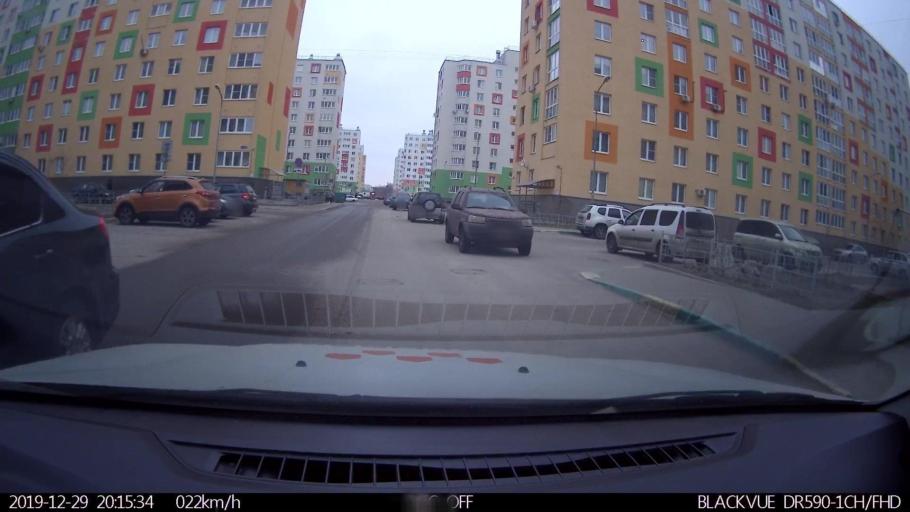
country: RU
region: Nizjnij Novgorod
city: Nizhniy Novgorod
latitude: 56.3422
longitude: 43.9116
